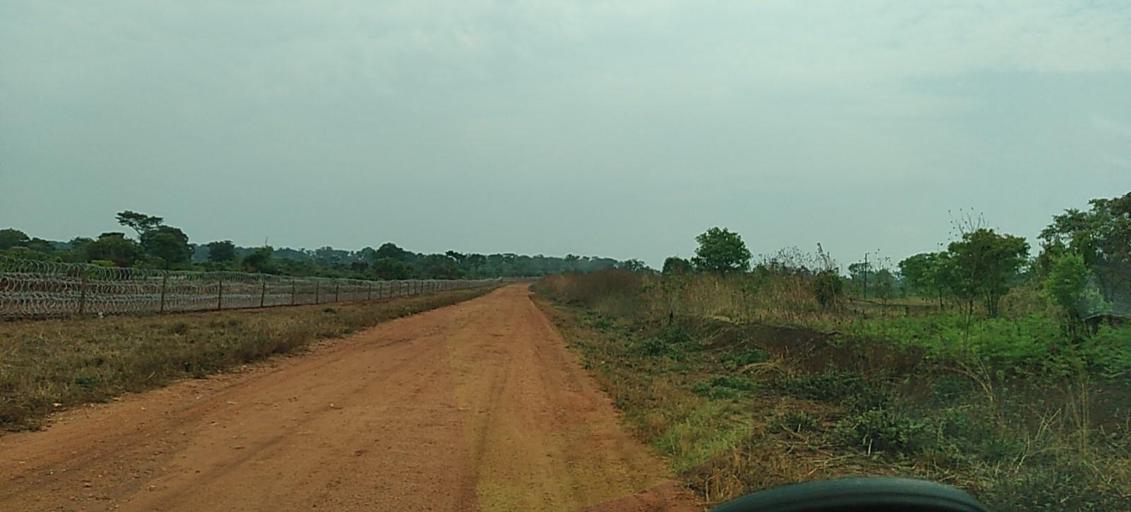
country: ZM
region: North-Western
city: Kansanshi
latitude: -12.1048
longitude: 26.4907
